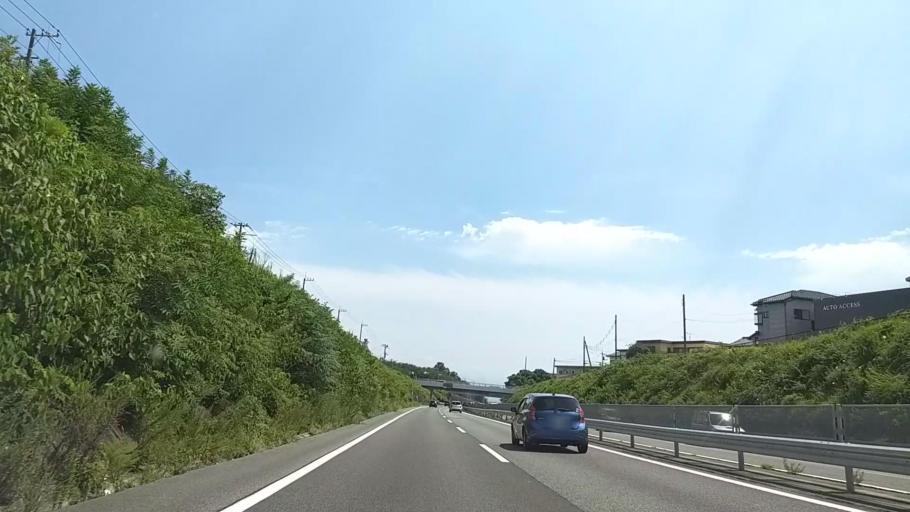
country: JP
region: Shizuoka
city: Fuji
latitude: 35.1897
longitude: 138.6736
